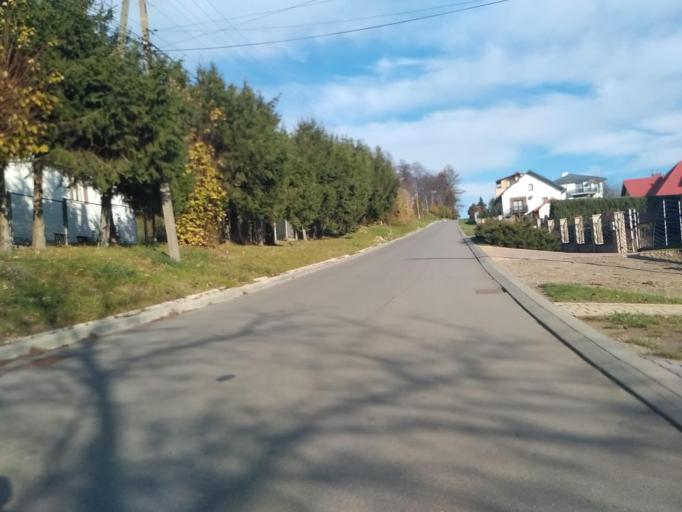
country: PL
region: Subcarpathian Voivodeship
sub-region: Powiat brzozowski
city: Brzozow
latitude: 49.6905
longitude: 22.0099
